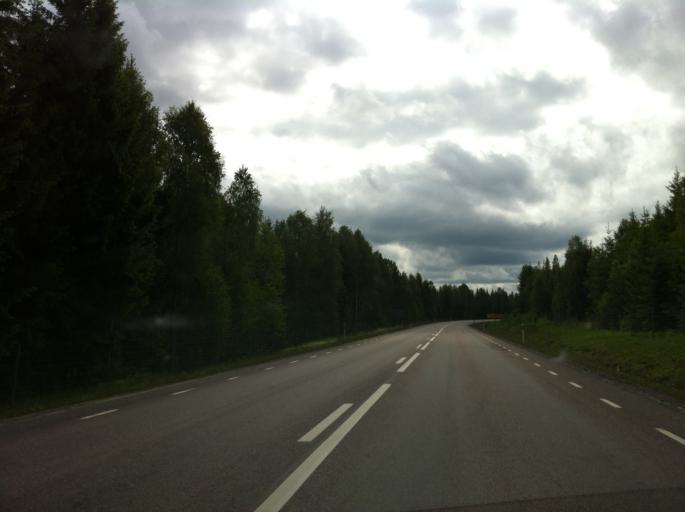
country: SE
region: Vaermland
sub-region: Sunne Kommun
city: Sunne
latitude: 59.7662
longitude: 13.1065
